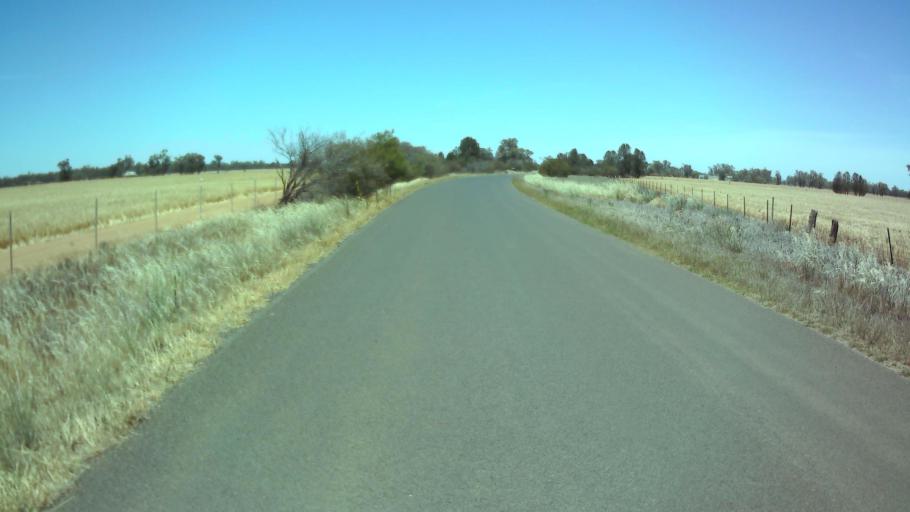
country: AU
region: New South Wales
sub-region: Weddin
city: Grenfell
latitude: -34.0554
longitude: 147.7808
